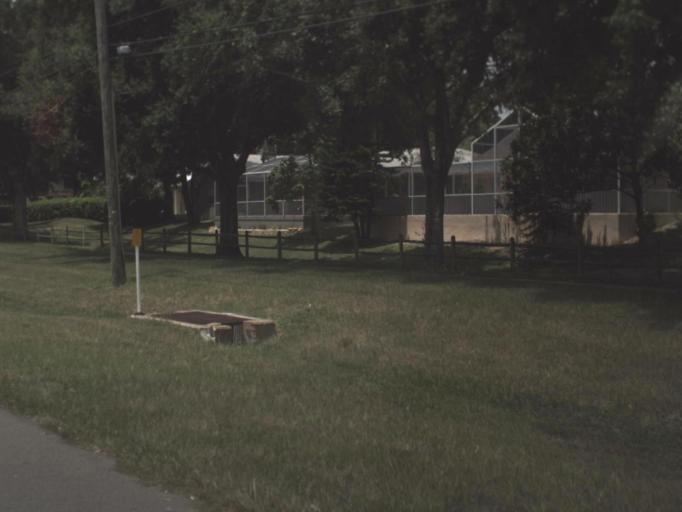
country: US
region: Florida
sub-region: Pinellas County
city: Palm Harbor
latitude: 28.0494
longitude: -82.7667
